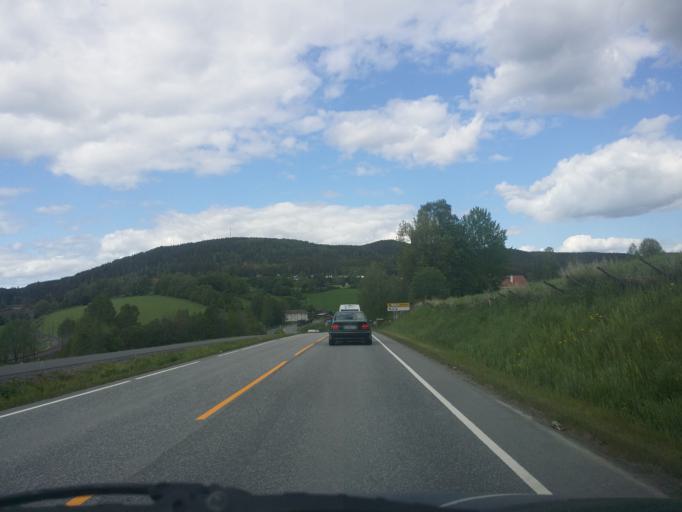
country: NO
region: Oppland
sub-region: Jevnaker
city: Jevnaker
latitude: 60.2512
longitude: 10.4271
